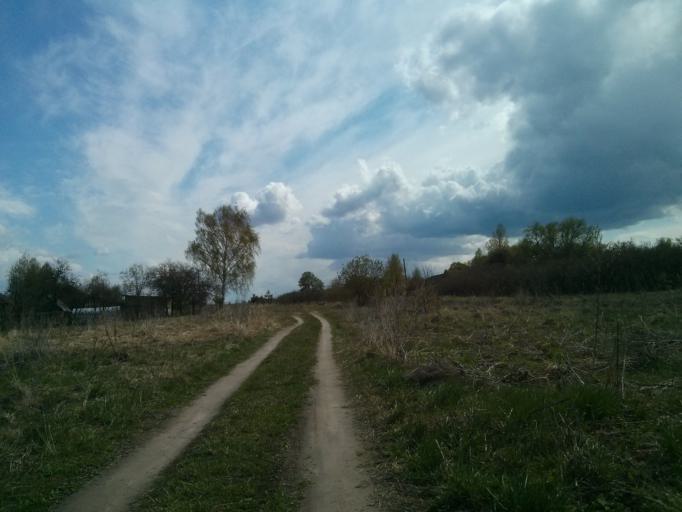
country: RU
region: Nizjnij Novgorod
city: Shimorskoye
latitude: 55.3039
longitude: 41.8456
